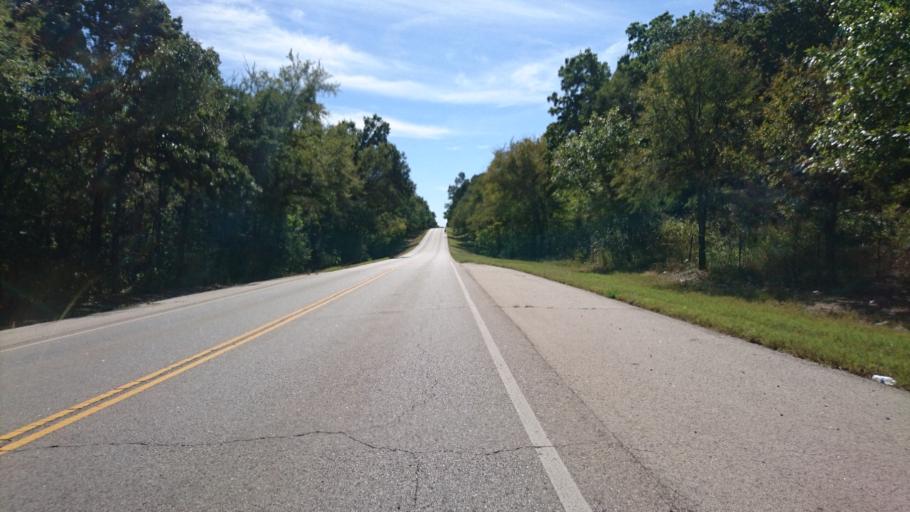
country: US
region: Oklahoma
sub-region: Lincoln County
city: Stroud
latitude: 35.7340
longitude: -96.7223
